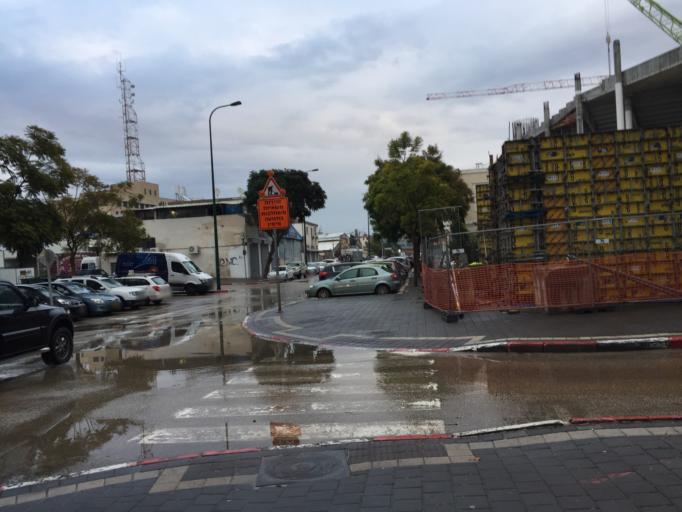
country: IL
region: Tel Aviv
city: Yafo
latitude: 32.0527
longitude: 34.7600
